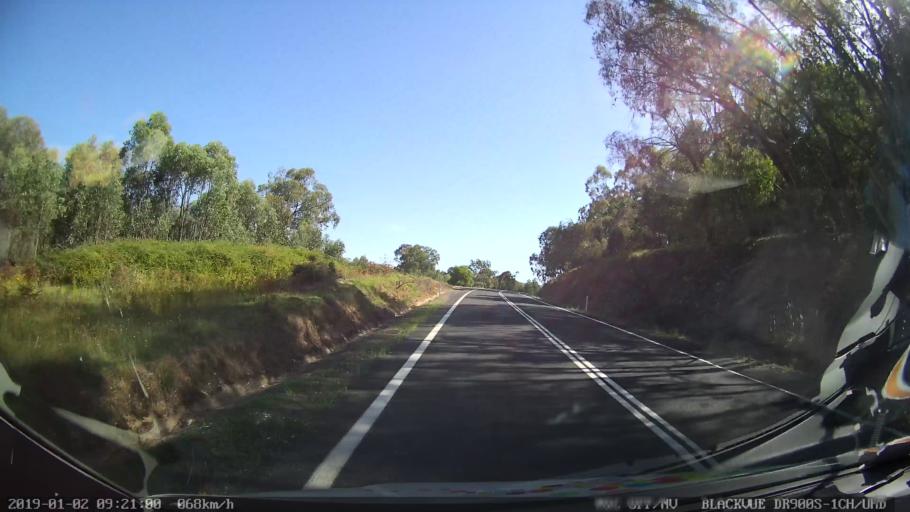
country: AU
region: New South Wales
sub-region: Tumut Shire
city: Tumut
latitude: -35.4103
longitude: 148.2894
